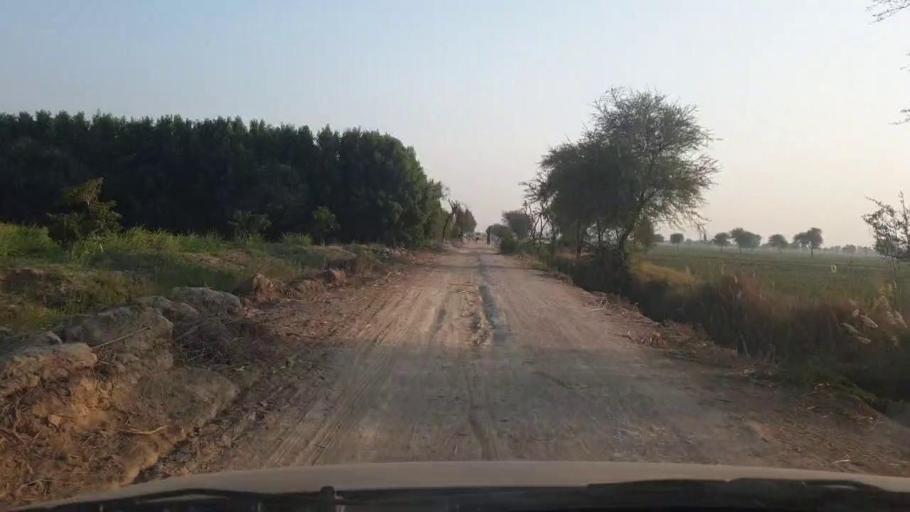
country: PK
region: Sindh
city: Mirwah Gorchani
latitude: 25.3565
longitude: 69.1528
